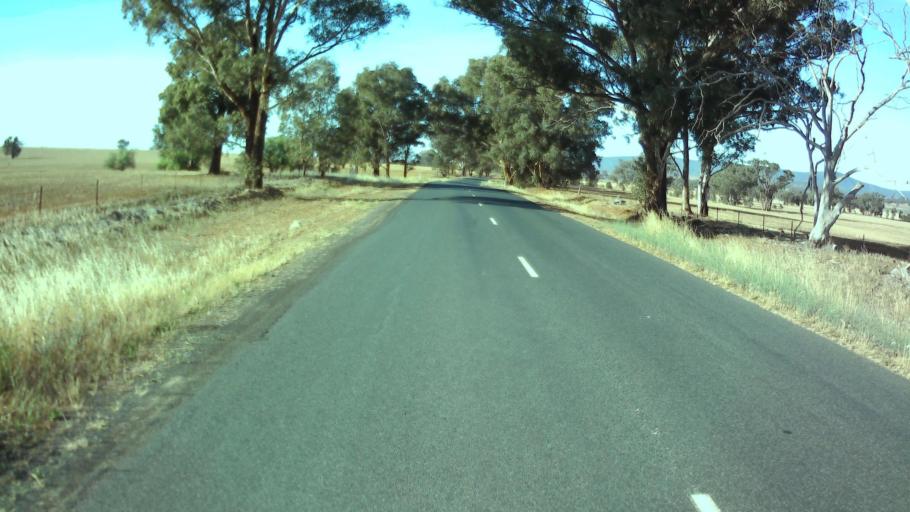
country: AU
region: New South Wales
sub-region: Weddin
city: Grenfell
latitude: -33.9162
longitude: 148.1423
